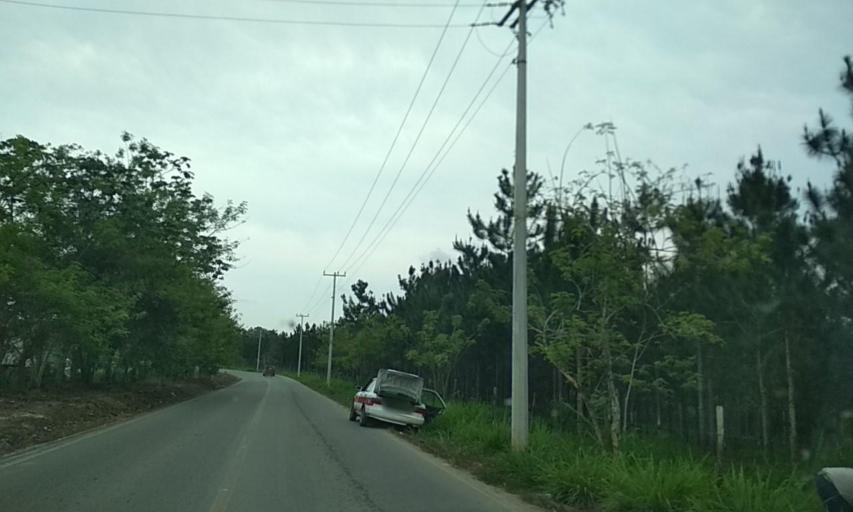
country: MX
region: Veracruz
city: Las Choapas
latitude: 17.8580
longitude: -94.1013
